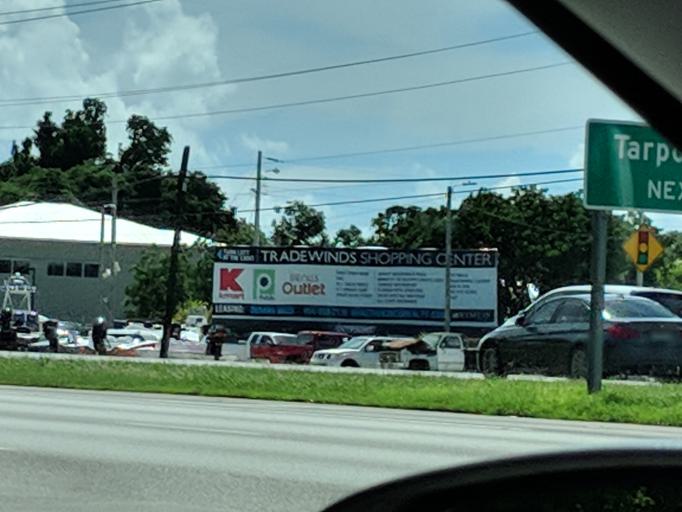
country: US
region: Florida
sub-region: Monroe County
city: Key Largo
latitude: 25.1144
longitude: -80.4212
